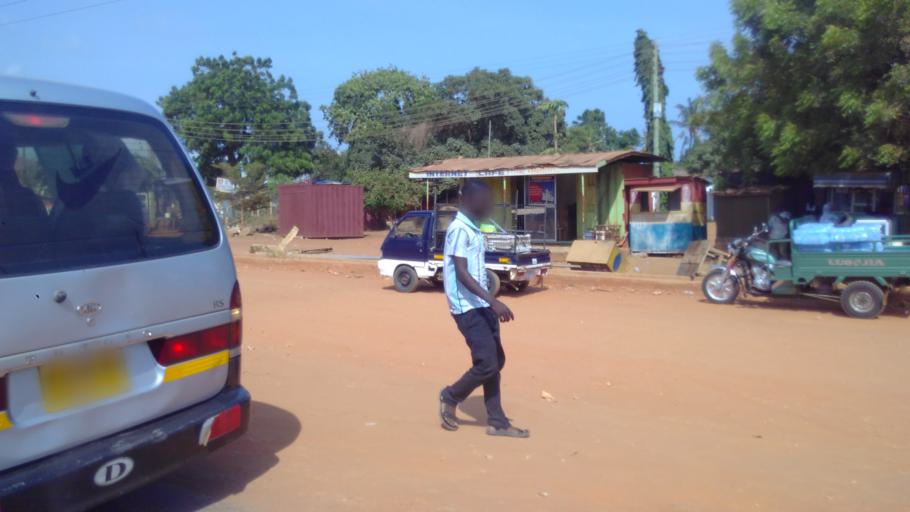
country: GH
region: Greater Accra
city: Nungua
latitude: 5.6326
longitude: -0.0652
